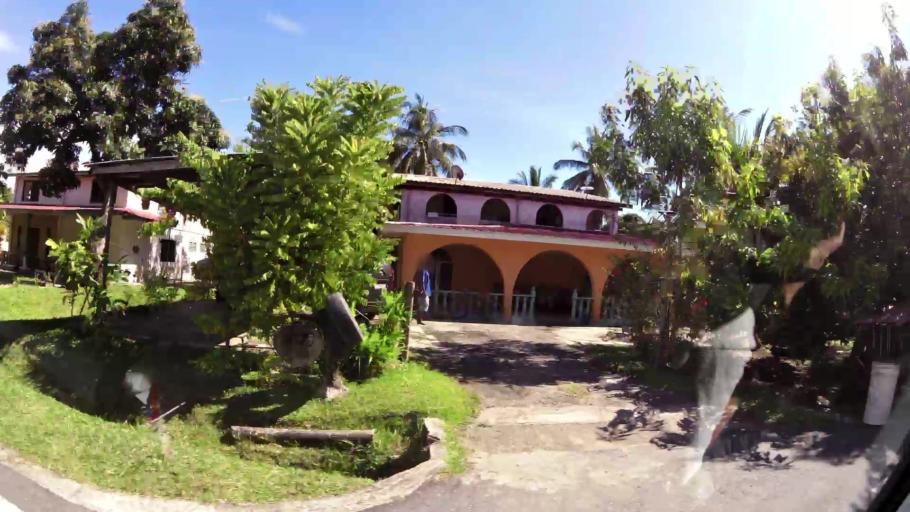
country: BN
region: Brunei and Muara
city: Bandar Seri Begawan
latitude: 5.0038
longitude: 115.0514
